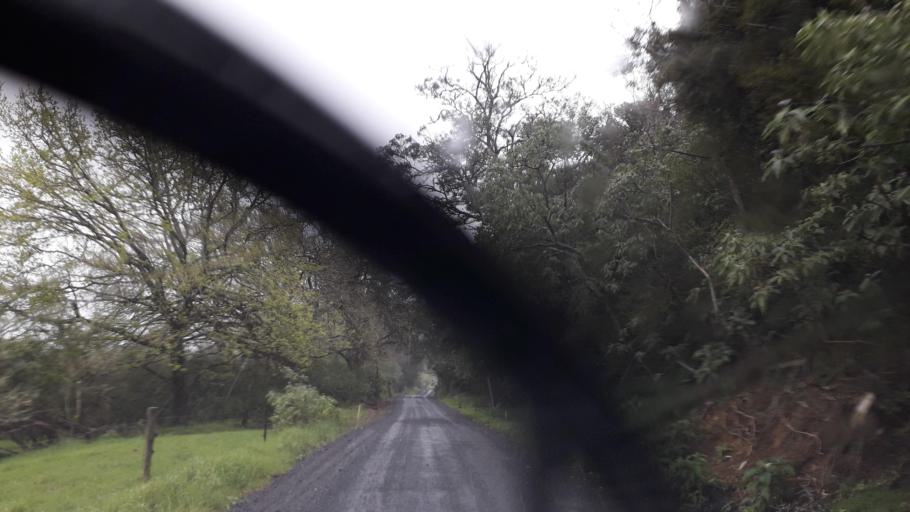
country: NZ
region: Northland
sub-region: Far North District
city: Waimate North
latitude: -35.4797
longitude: 173.6974
